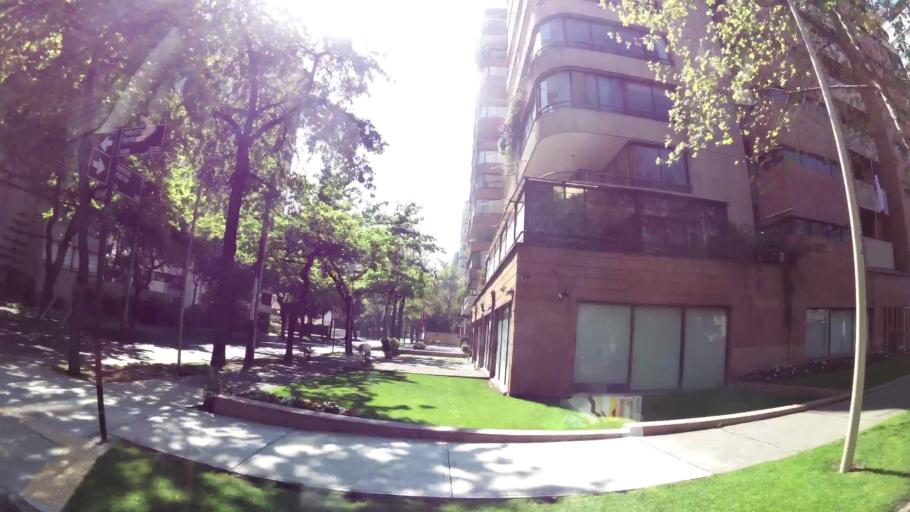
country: CL
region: Santiago Metropolitan
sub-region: Provincia de Santiago
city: Villa Presidente Frei, Nunoa, Santiago, Chile
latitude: -33.4191
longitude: -70.5932
